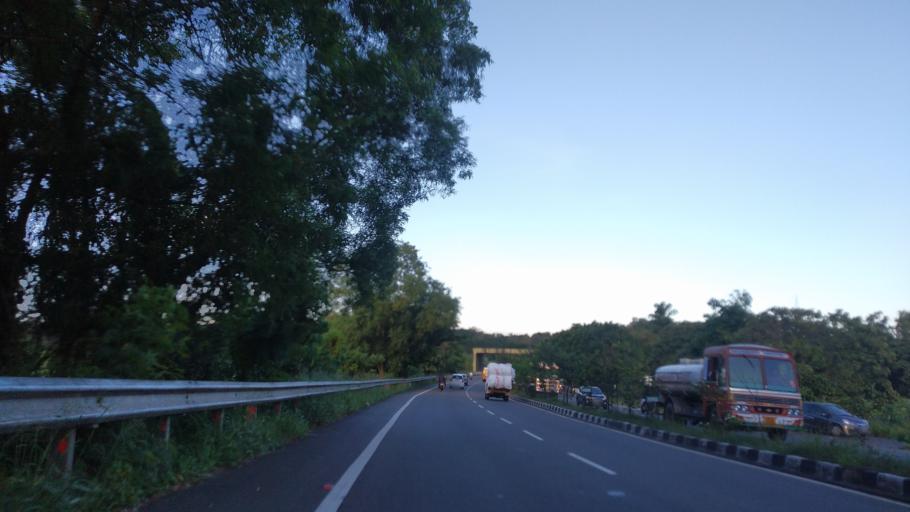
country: IN
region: Kerala
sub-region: Ernakulam
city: Elur
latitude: 10.0685
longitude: 76.3007
